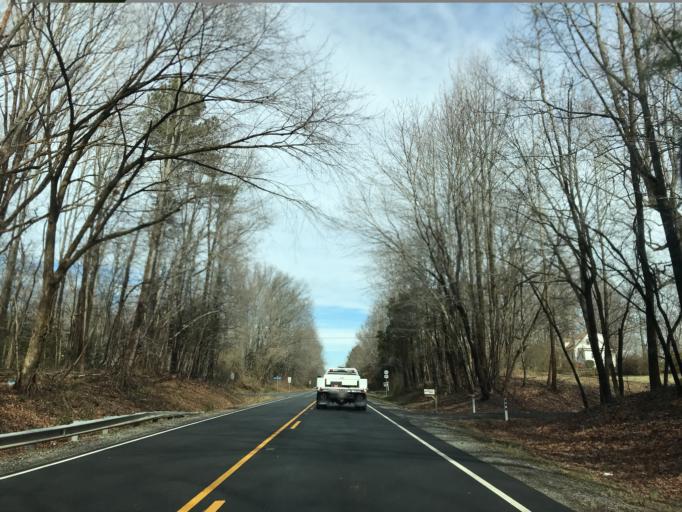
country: US
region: Virginia
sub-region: King George County
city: Dahlgren
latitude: 38.3165
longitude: -77.0795
